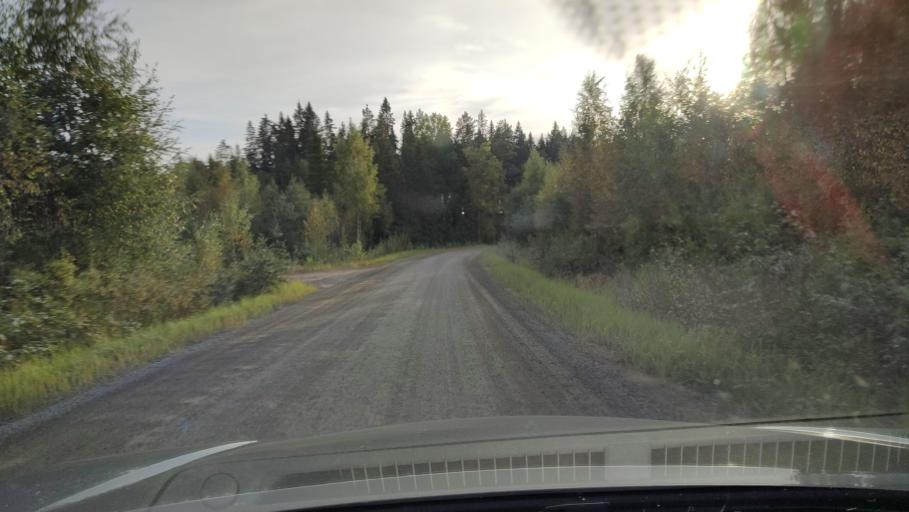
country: FI
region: Southern Ostrobothnia
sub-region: Suupohja
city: Karijoki
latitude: 62.1245
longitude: 21.6034
